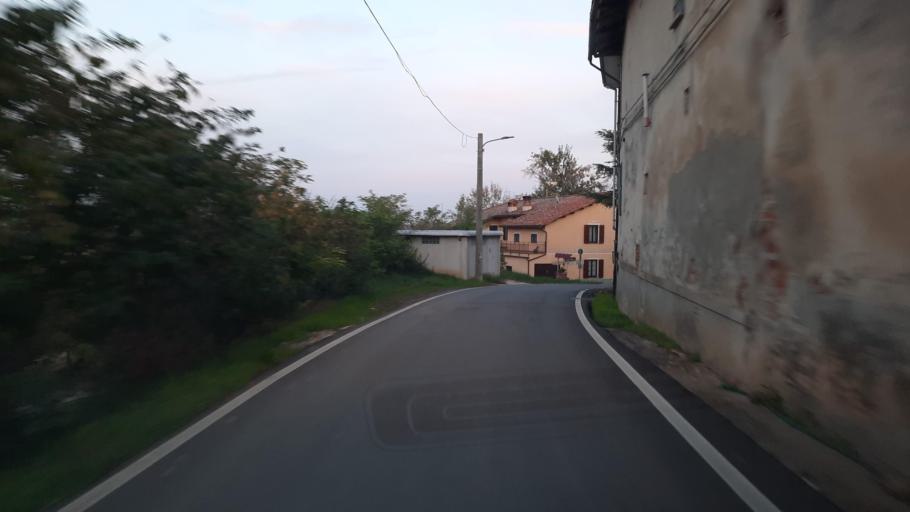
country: IT
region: Piedmont
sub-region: Provincia di Asti
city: Tonco
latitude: 45.0249
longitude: 8.1941
